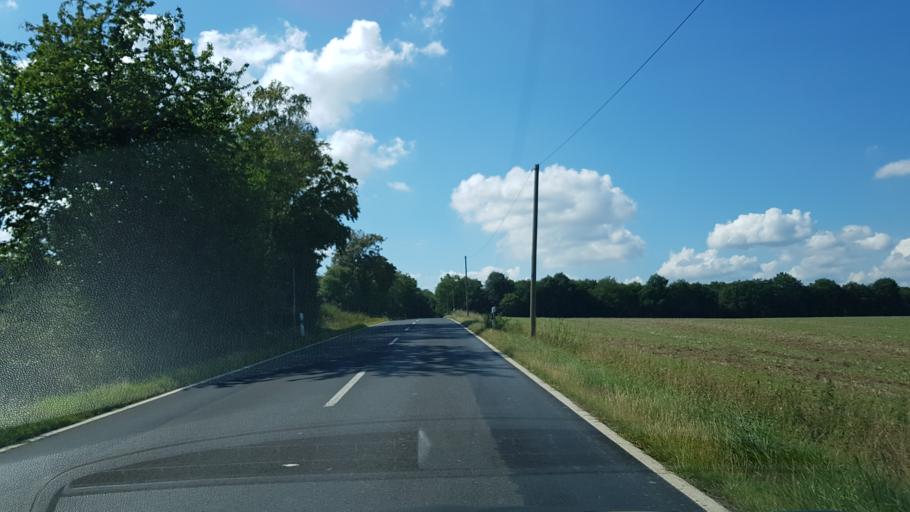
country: DE
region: Rheinland-Pfalz
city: Pommern
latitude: 50.1537
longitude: 7.2685
